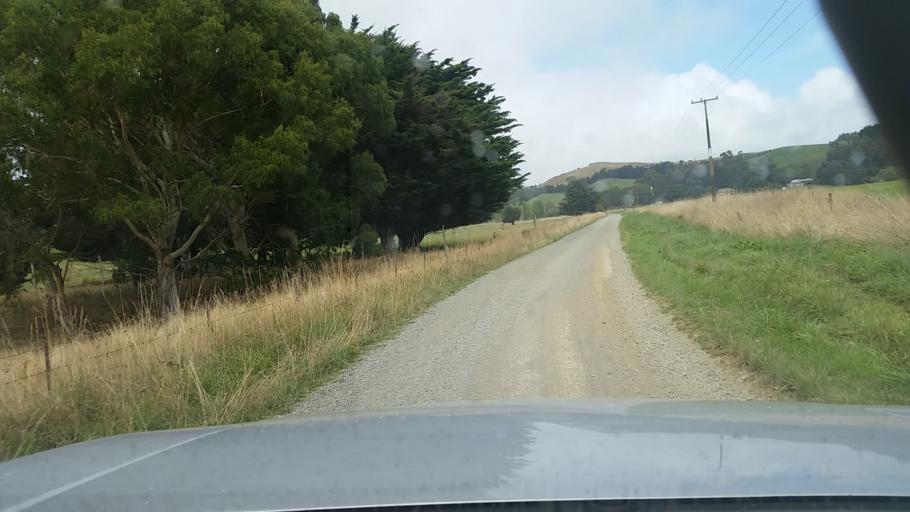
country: NZ
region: Marlborough
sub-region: Marlborough District
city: Blenheim
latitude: -41.7253
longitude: 173.9251
